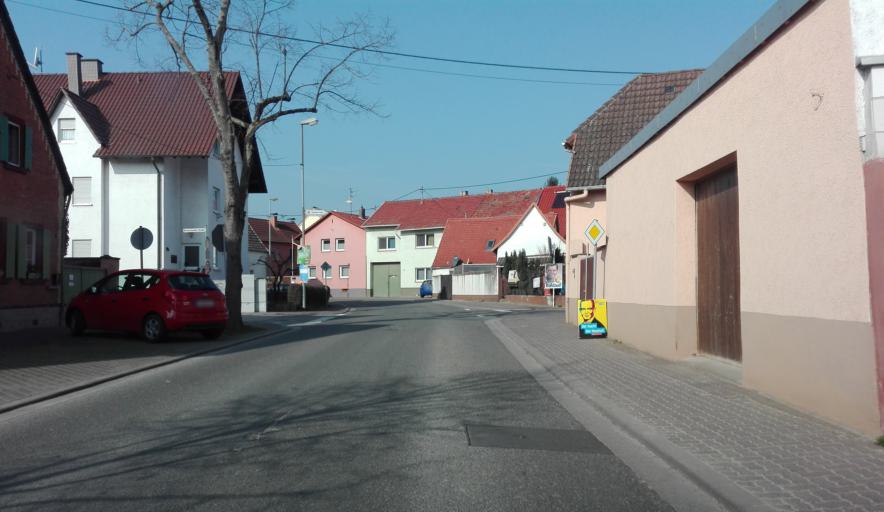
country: DE
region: Rheinland-Pfalz
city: Kleinniedesheim
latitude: 49.5878
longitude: 8.3254
